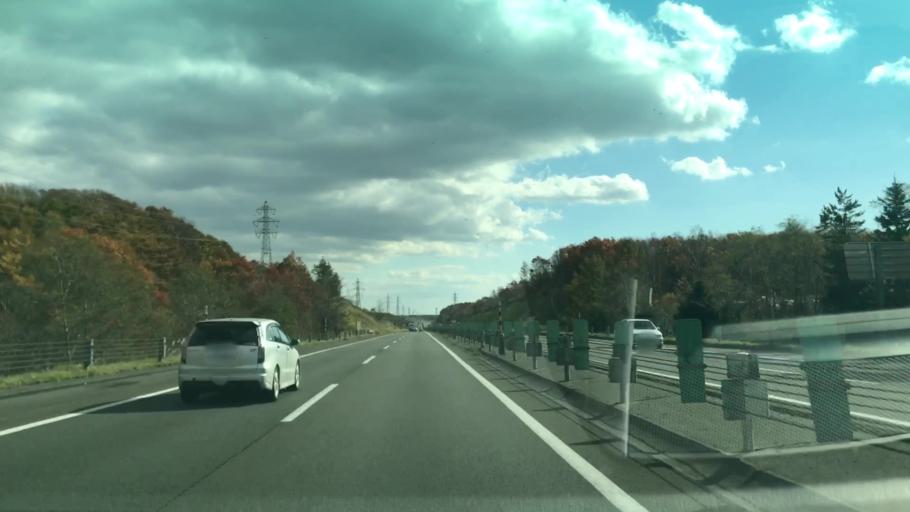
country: JP
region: Hokkaido
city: Kitahiroshima
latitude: 42.9633
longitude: 141.4972
